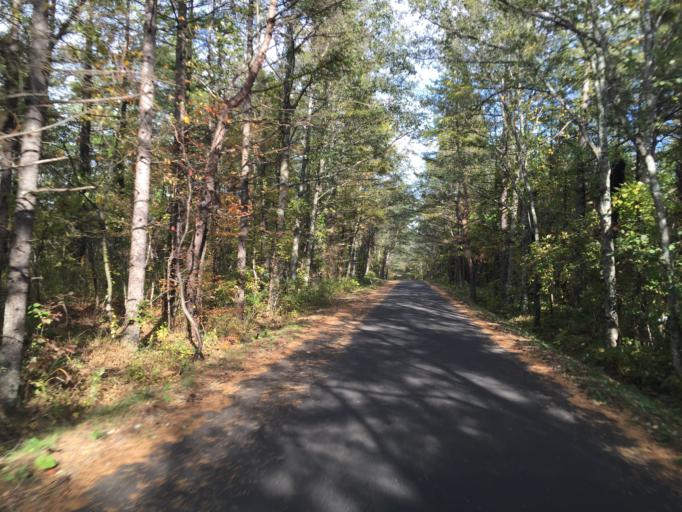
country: JP
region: Fukushima
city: Fukushima-shi
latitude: 37.7101
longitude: 140.3250
